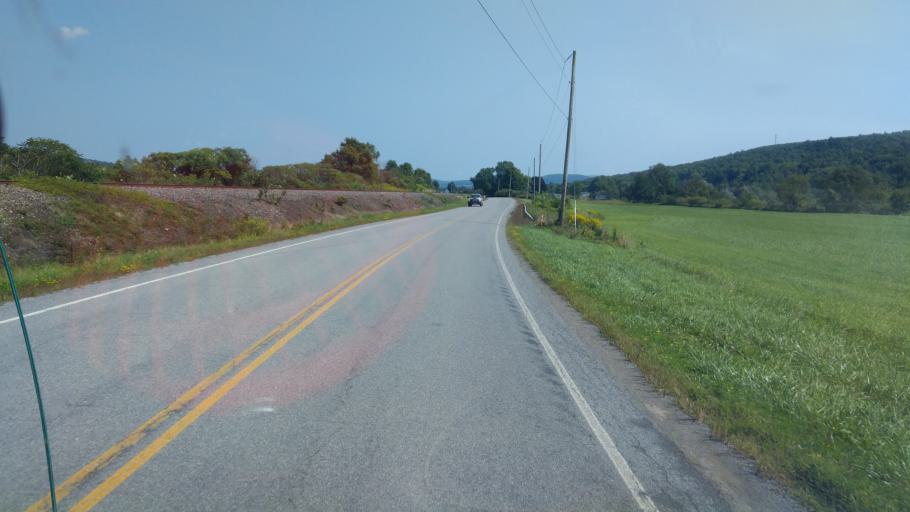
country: US
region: New York
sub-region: Allegany County
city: Belmont
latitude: 42.2316
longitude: -78.0868
